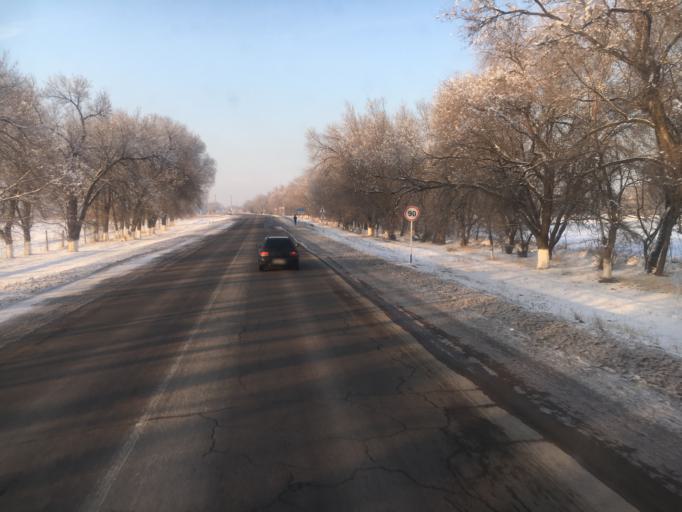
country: KZ
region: Almaty Oblysy
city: Burunday
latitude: 43.3287
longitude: 76.6623
